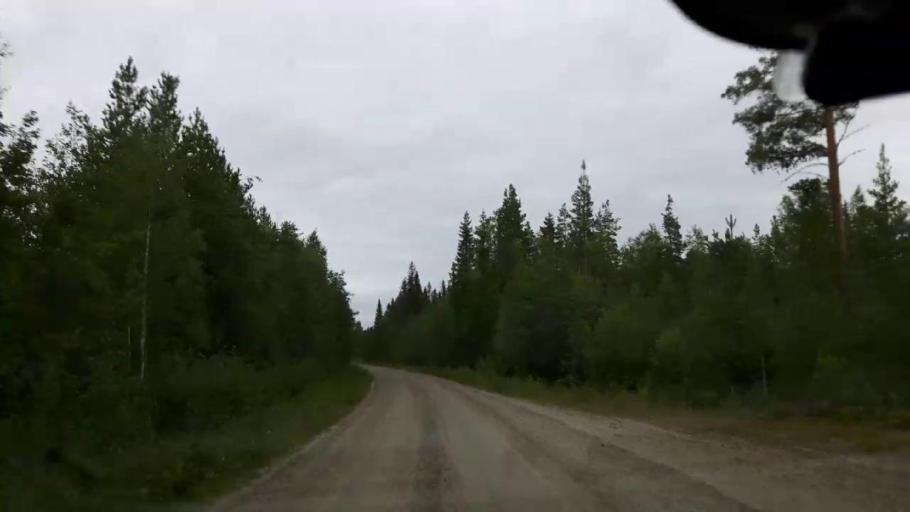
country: SE
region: Vaesternorrland
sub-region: Ange Kommun
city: Ange
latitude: 62.8113
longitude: 15.7263
